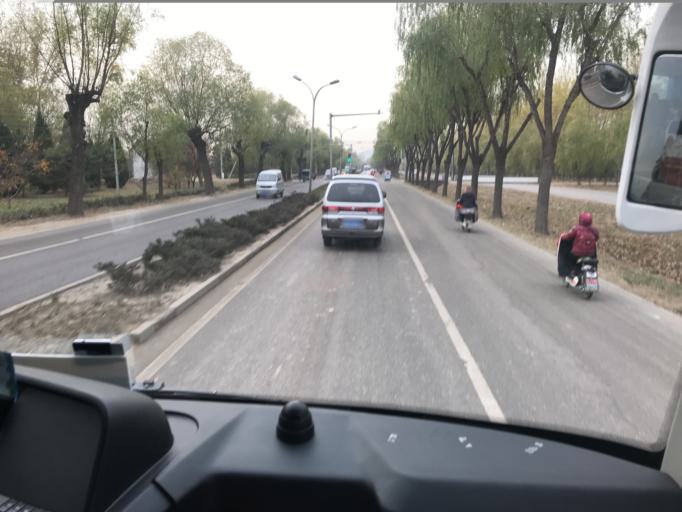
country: CN
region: Beijing
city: Wenquan
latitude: 40.0872
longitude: 116.2101
